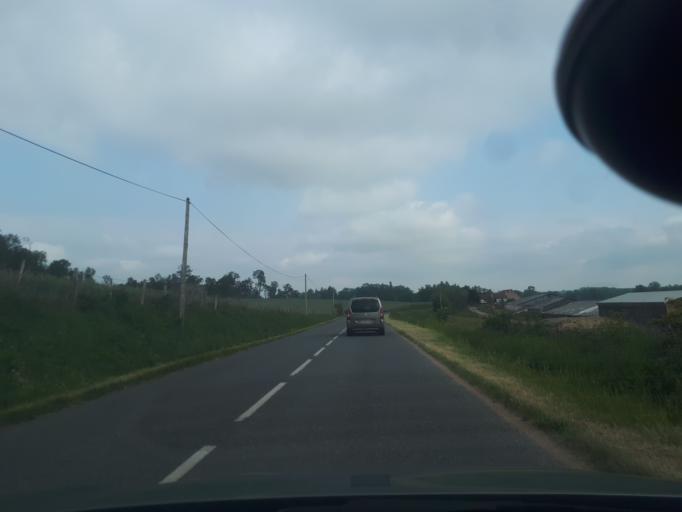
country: FR
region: Auvergne
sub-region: Departement de l'Allier
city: Lapalisse
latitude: 46.3074
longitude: 3.5960
